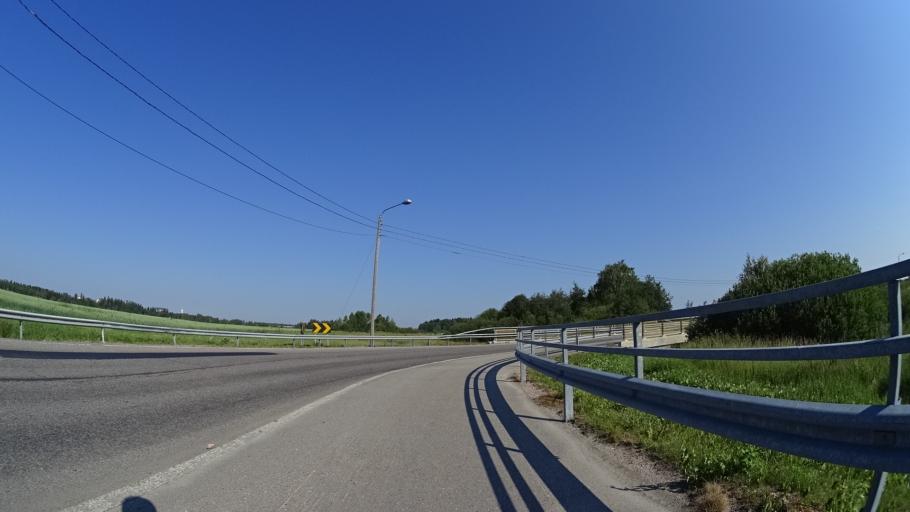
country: FI
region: Uusimaa
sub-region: Helsinki
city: Vantaa
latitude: 60.3036
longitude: 25.0657
